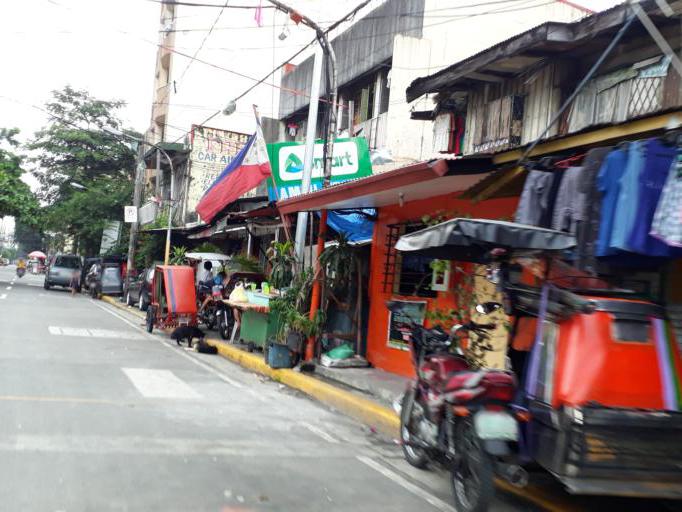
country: PH
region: Metro Manila
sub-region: City of Manila
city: Manila
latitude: 14.6094
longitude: 120.9973
